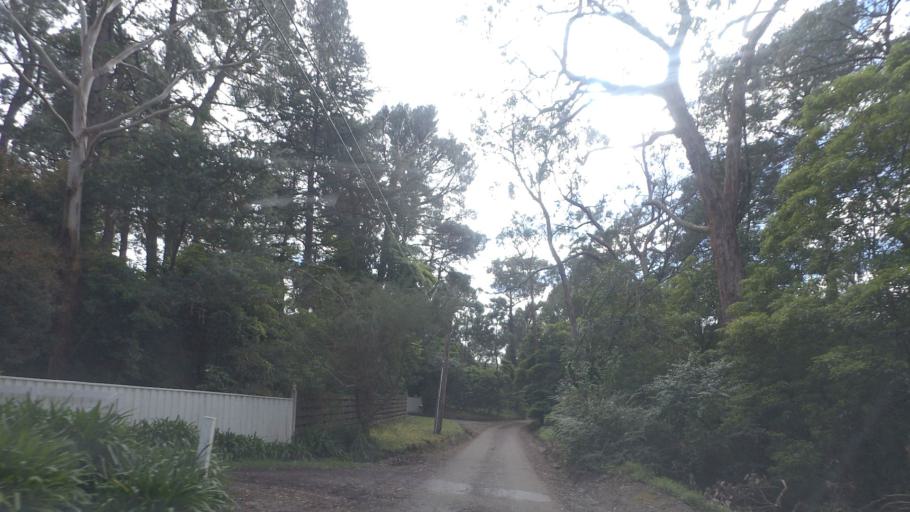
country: AU
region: Victoria
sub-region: Maroondah
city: Croydon South
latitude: -37.8055
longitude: 145.2601
